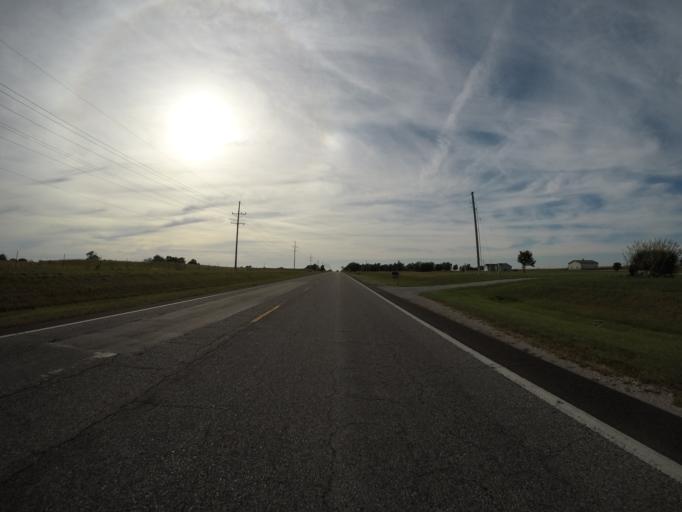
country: US
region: Kansas
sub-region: Franklin County
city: Wellsville
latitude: 38.7679
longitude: -95.1070
